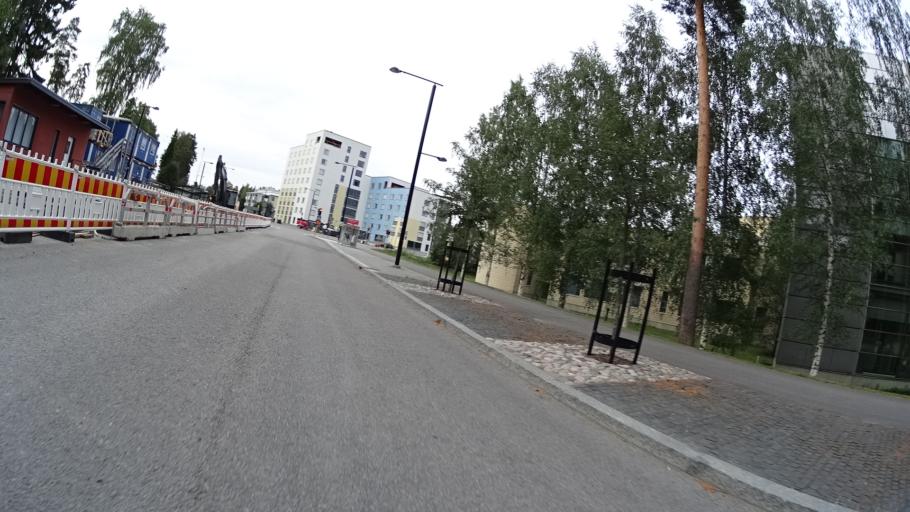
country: FI
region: Uusimaa
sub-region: Helsinki
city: Teekkarikylae
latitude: 60.2584
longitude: 24.8436
